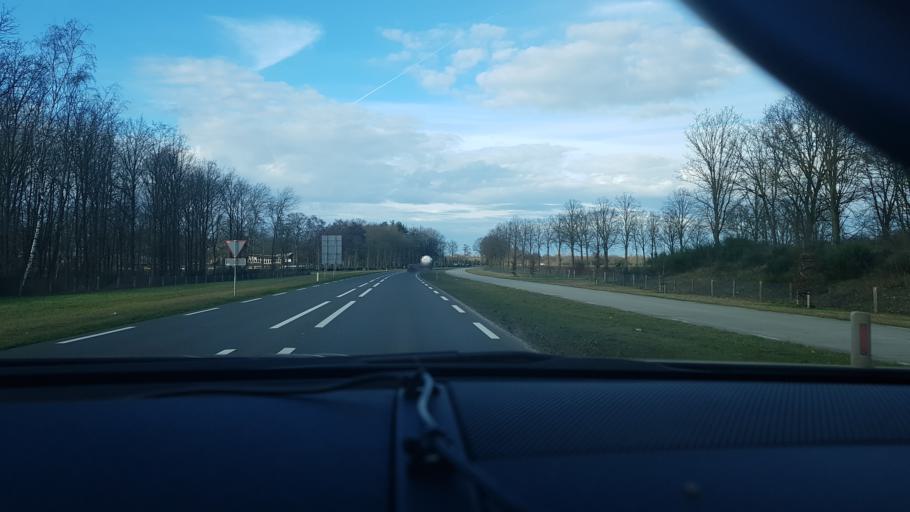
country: NL
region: Limburg
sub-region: Gemeente Peel en Maas
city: Maasbree
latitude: 51.3532
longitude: 6.0124
